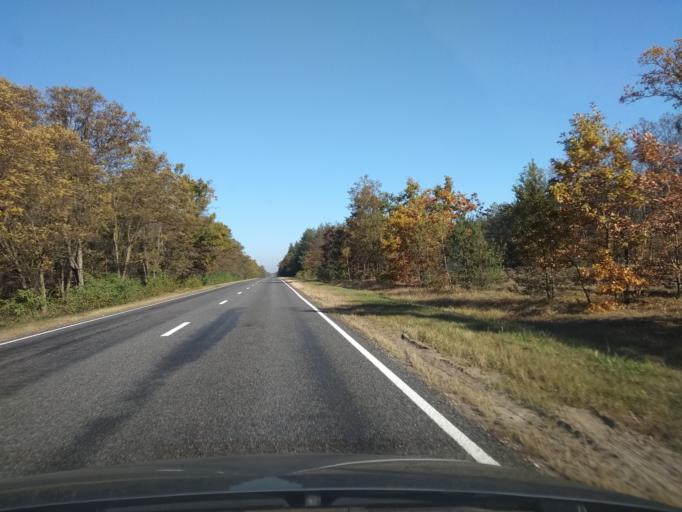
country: BY
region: Brest
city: Malaryta
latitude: 51.9673
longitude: 24.1956
